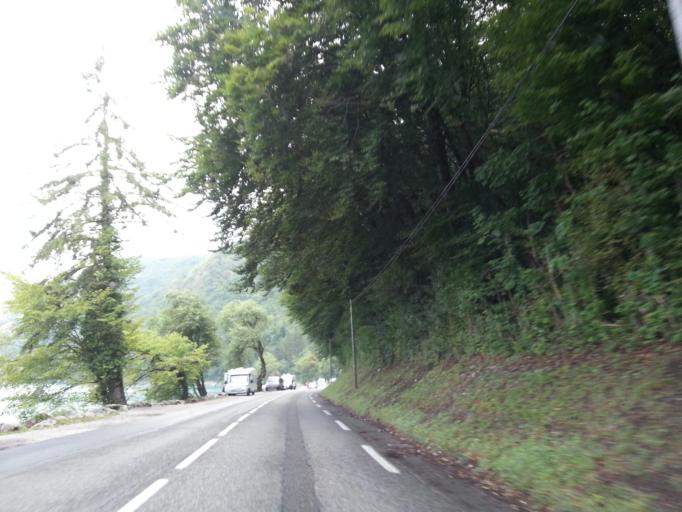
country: FR
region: Rhone-Alpes
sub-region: Departement de la Haute-Savoie
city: Doussard
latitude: 45.8027
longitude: 6.2298
